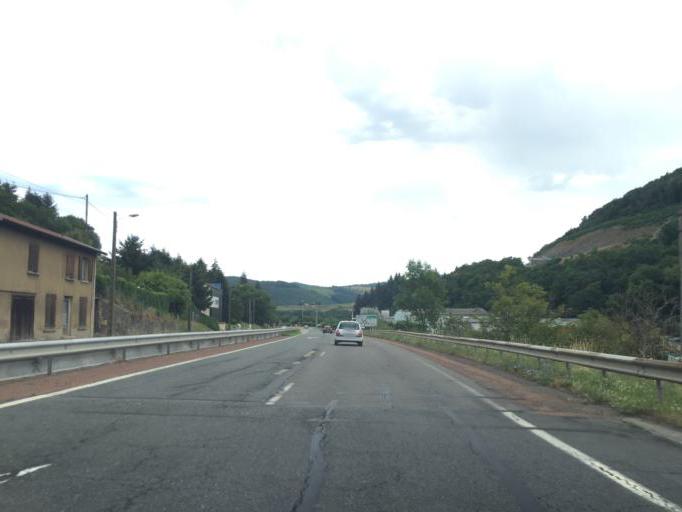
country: FR
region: Rhone-Alpes
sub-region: Departement du Rhone
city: Pontcharra-sur-Turdine
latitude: 45.8821
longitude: 4.4719
